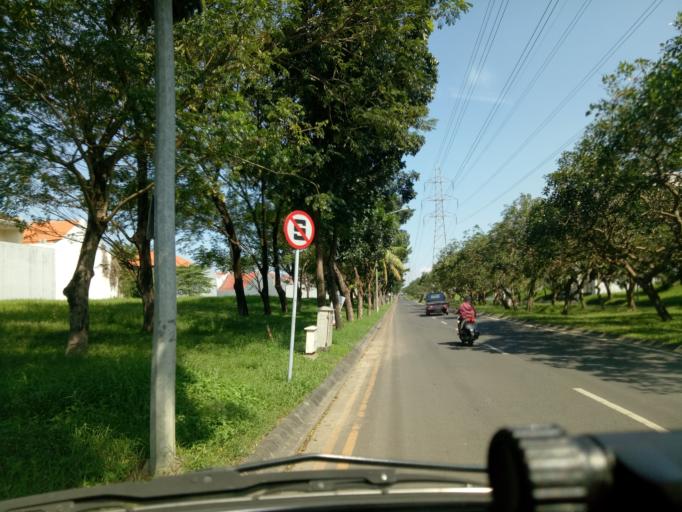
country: ID
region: East Java
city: Driyorejo
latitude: -7.2844
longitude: 112.6471
